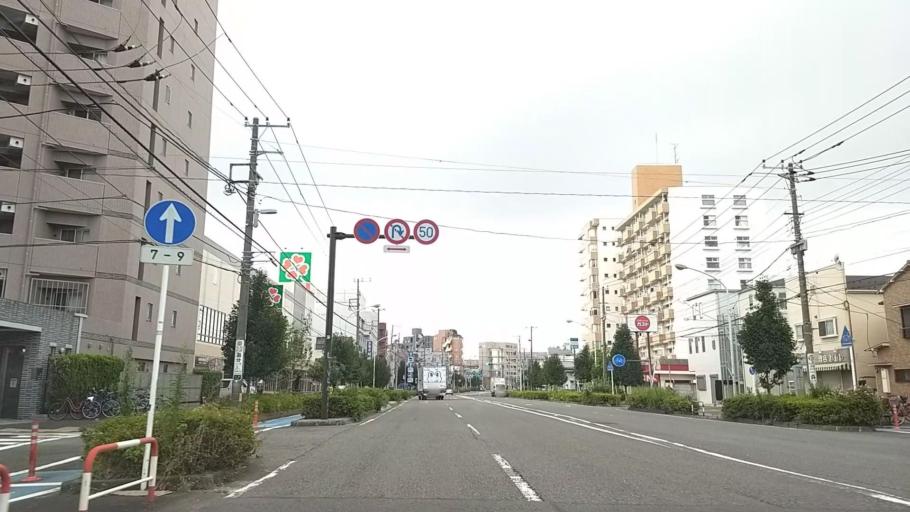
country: JP
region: Kanagawa
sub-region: Kawasaki-shi
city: Kawasaki
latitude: 35.5247
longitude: 139.7134
